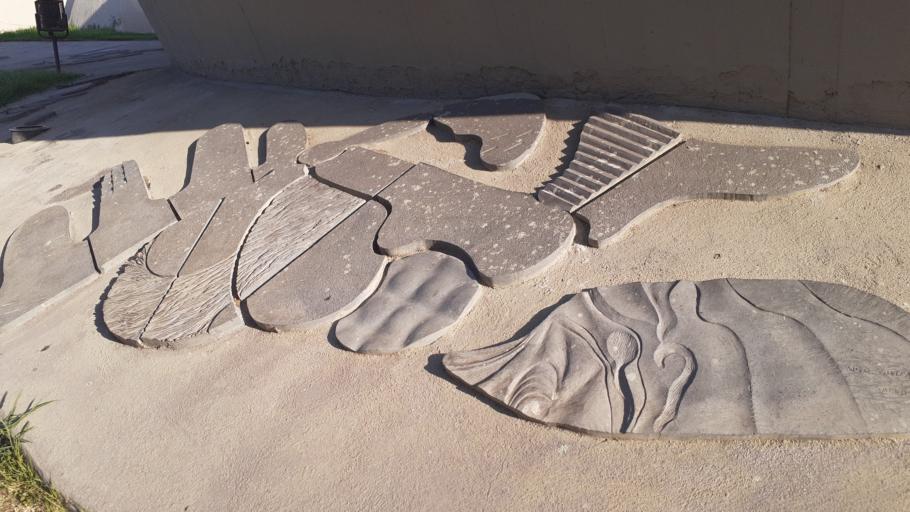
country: IT
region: Sicily
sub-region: Catania
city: Cerza
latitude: 37.5205
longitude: 15.1120
